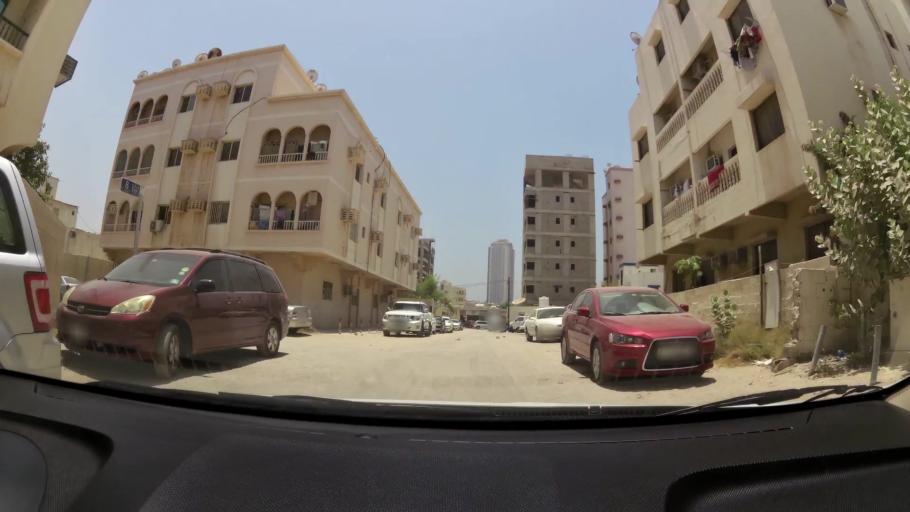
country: AE
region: Ajman
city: Ajman
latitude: 25.4088
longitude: 55.4418
